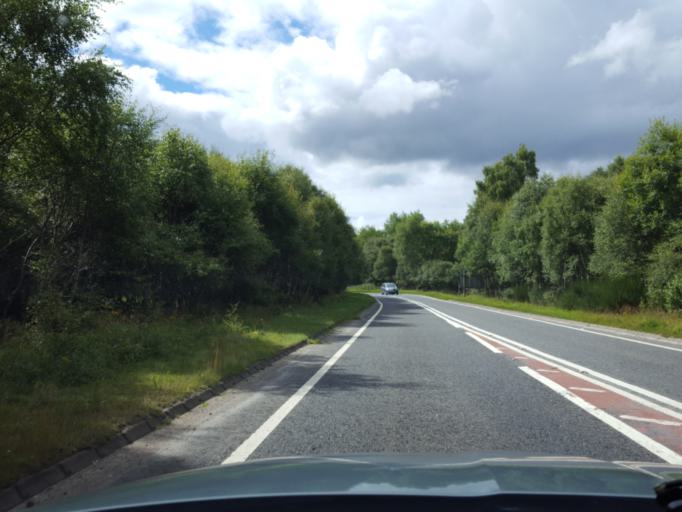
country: GB
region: Scotland
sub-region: Highland
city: Aviemore
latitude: 57.2138
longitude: -3.8203
